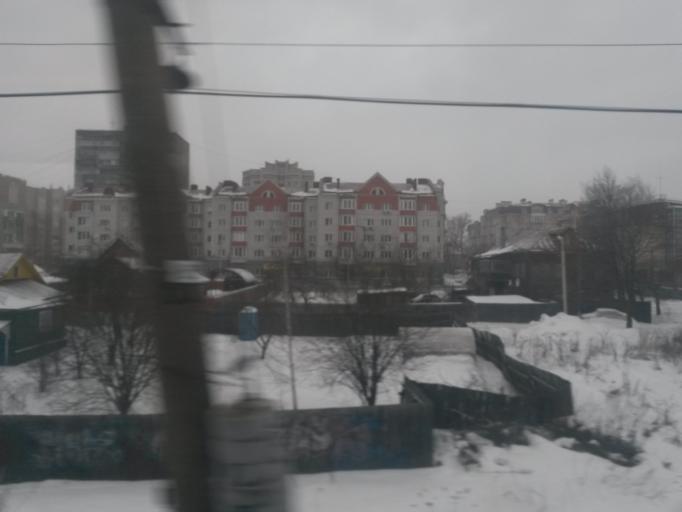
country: RU
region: Moskovskaya
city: Sergiyev Posad
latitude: 56.3022
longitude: 38.1339
